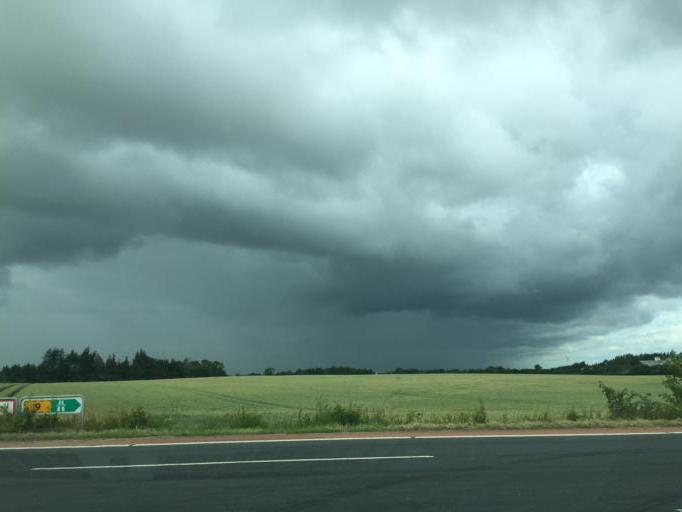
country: DK
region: South Denmark
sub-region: Faaborg-Midtfyn Kommune
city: Arslev
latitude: 55.2941
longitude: 10.4511
